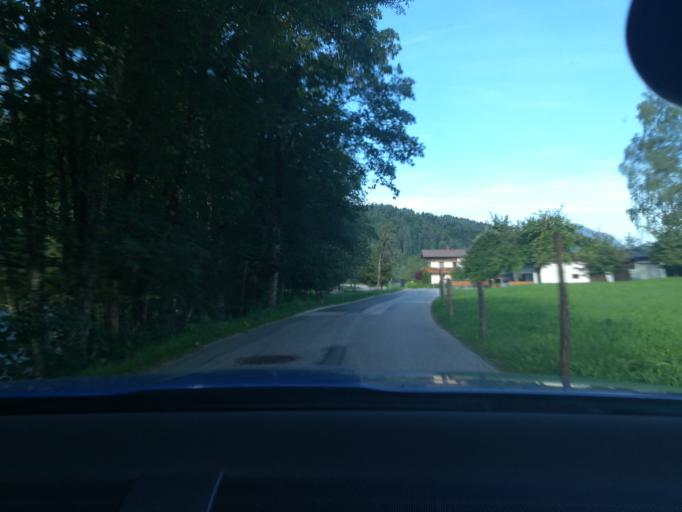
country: AT
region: Salzburg
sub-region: Politischer Bezirk Hallein
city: Abtenau
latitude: 47.5750
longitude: 13.3828
